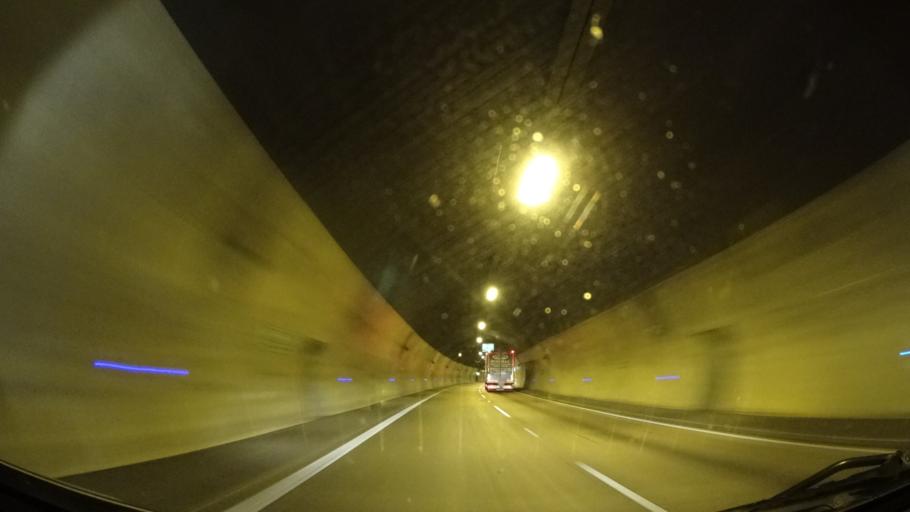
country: CZ
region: Ustecky
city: Libouchec
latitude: 50.7523
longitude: 13.9898
